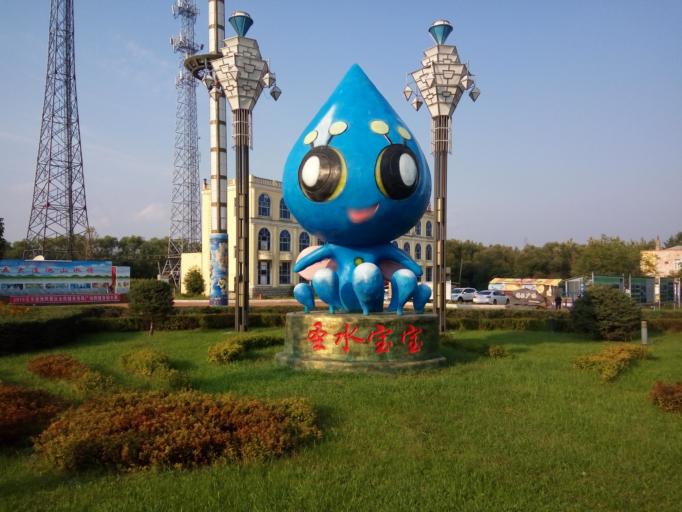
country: CN
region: Heilongjiang Sheng
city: Erjing
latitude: 48.6474
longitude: 126.1404
